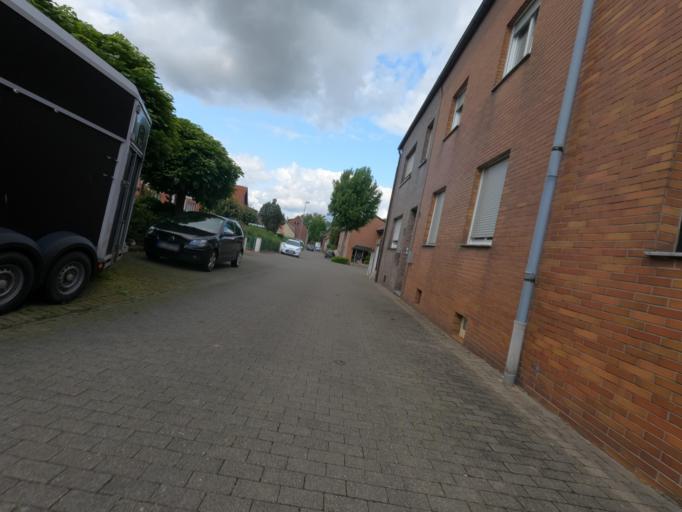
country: DE
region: North Rhine-Westphalia
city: Baesweiler
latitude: 50.9286
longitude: 6.1888
